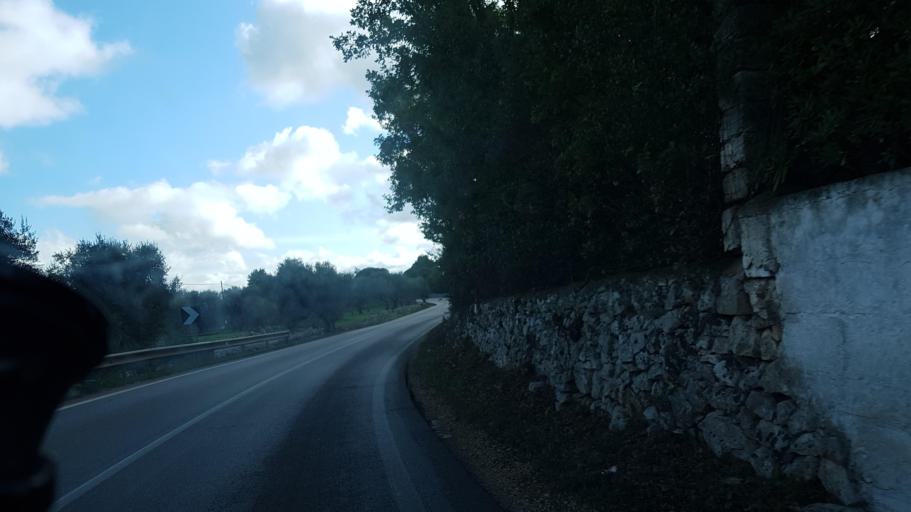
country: IT
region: Apulia
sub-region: Provincia di Brindisi
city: Ostuni
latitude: 40.6798
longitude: 17.5907
